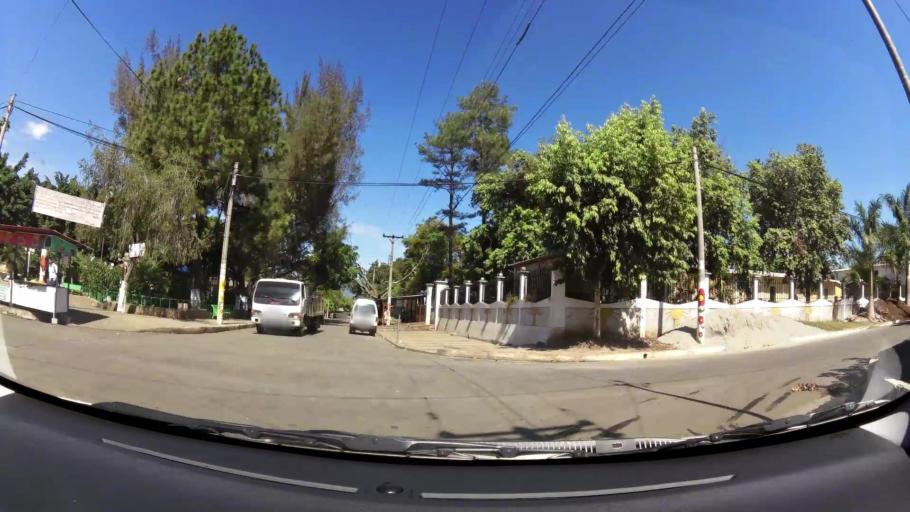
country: SV
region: Santa Ana
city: Chalchuapa
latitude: 13.9747
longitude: -89.7054
